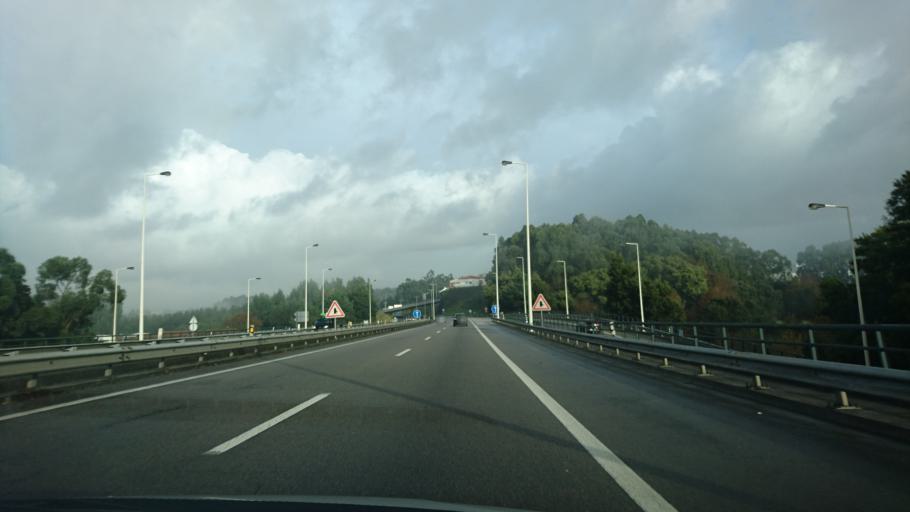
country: PT
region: Porto
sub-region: Gondomar
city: Gondomar
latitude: 41.1489
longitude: -8.5478
